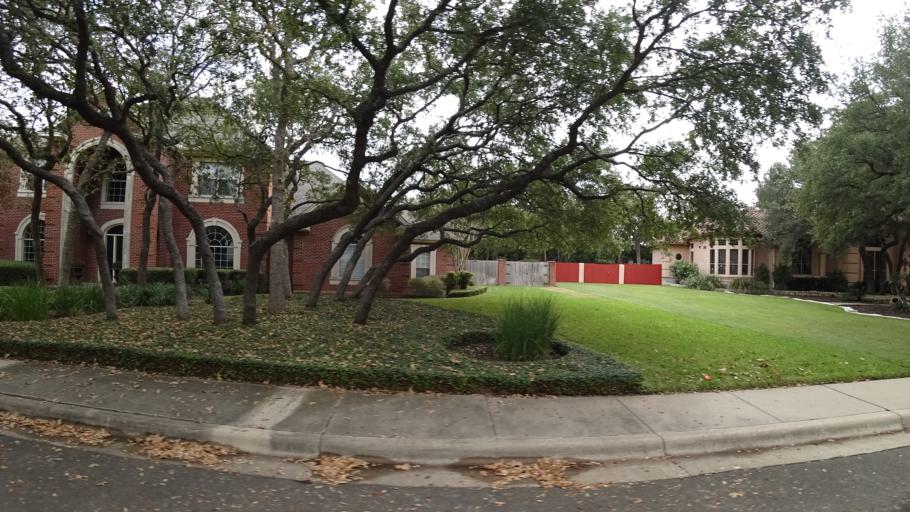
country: US
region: Texas
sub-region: Williamson County
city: Brushy Creek
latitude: 30.5139
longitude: -97.7118
